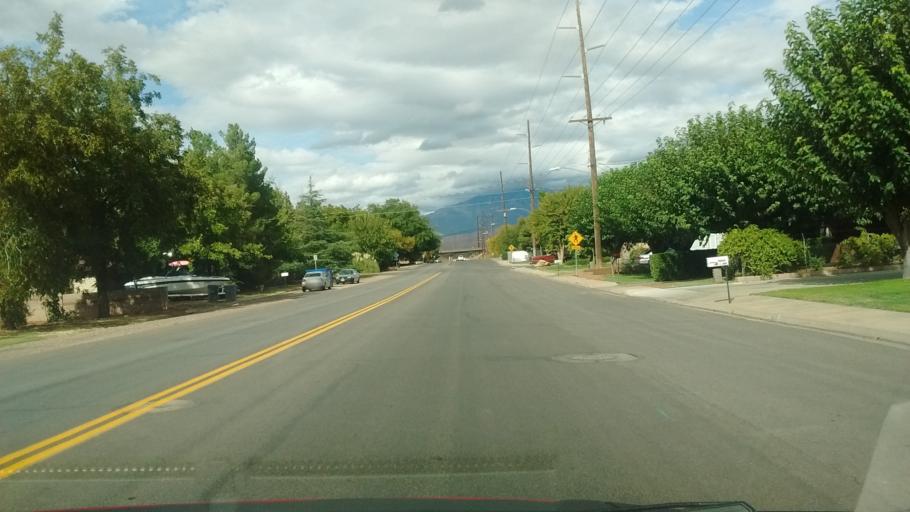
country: US
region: Utah
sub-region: Washington County
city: Washington
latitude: 37.1347
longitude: -113.5098
